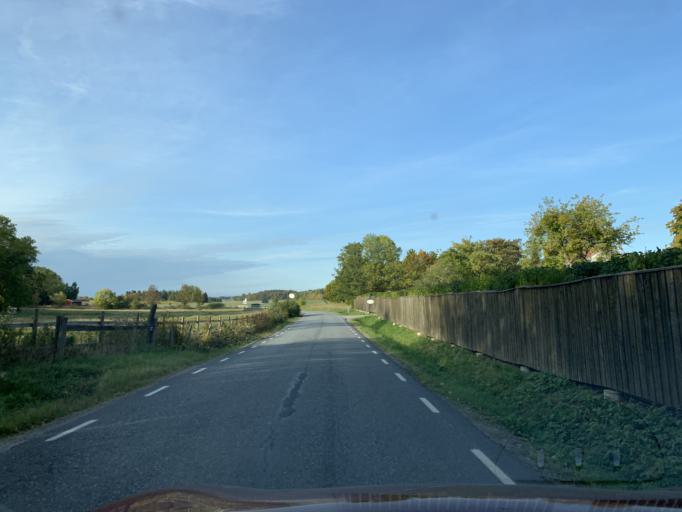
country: SE
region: Stockholm
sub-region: Upplands-Bro Kommun
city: Bro
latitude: 59.5047
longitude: 17.5857
